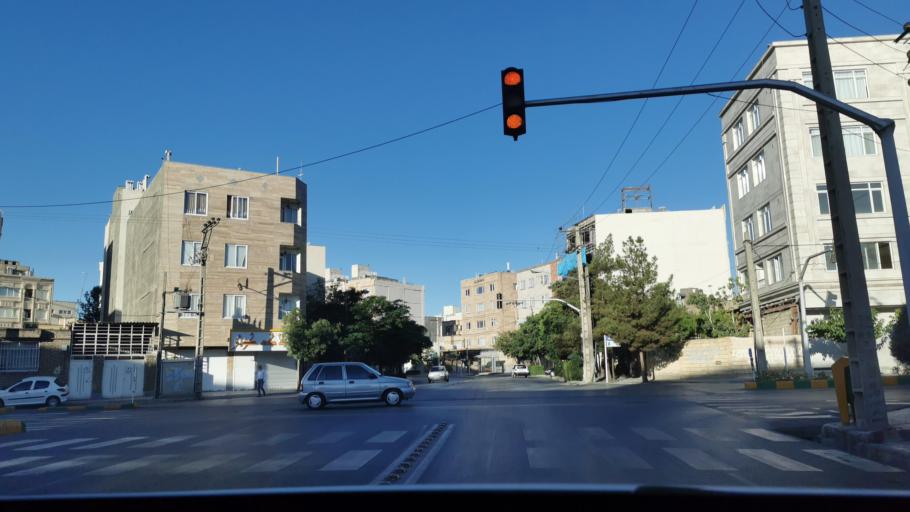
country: IR
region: Razavi Khorasan
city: Mashhad
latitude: 36.3585
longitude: 59.4983
